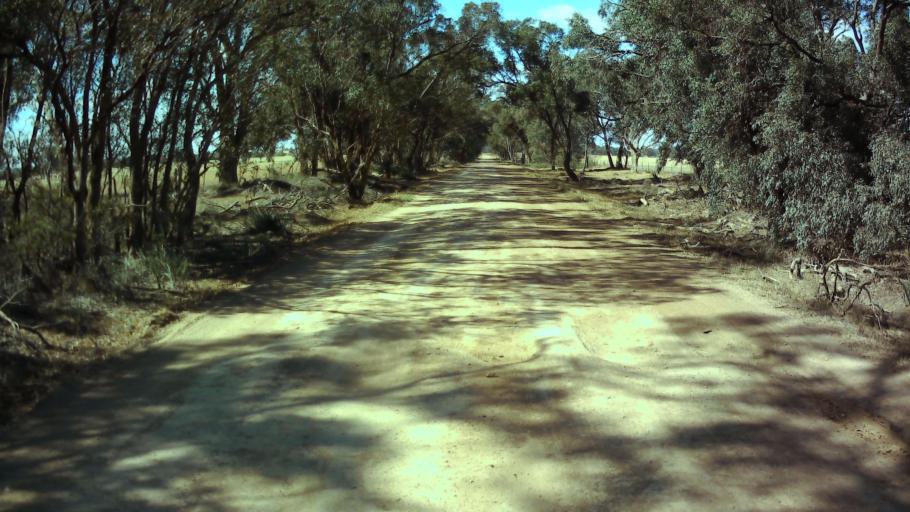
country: AU
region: New South Wales
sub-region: Weddin
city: Grenfell
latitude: -34.0504
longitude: 148.3140
